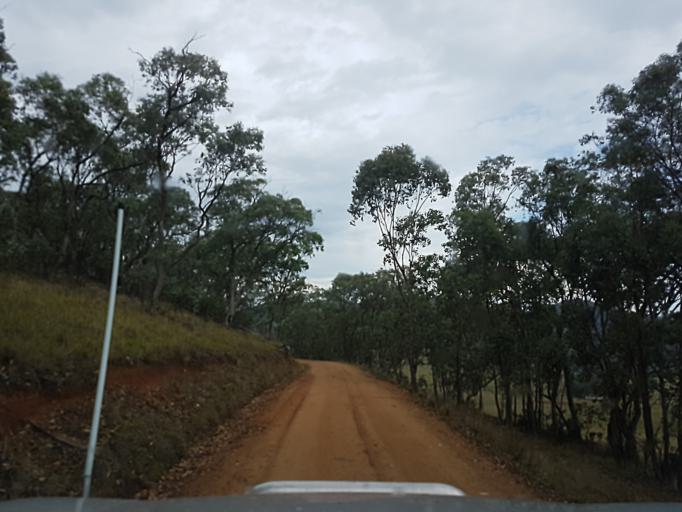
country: AU
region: New South Wales
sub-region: Snowy River
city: Jindabyne
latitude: -36.9568
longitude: 148.3666
